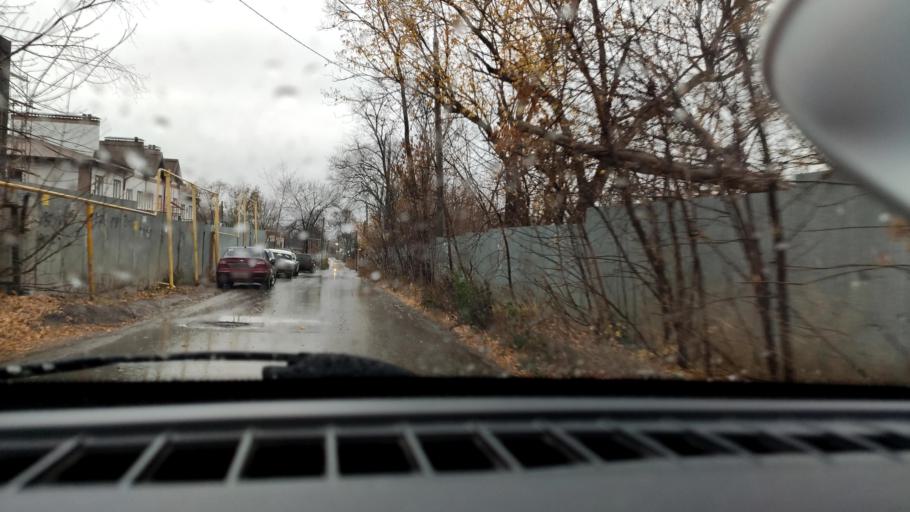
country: RU
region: Samara
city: Samara
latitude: 53.2329
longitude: 50.1763
